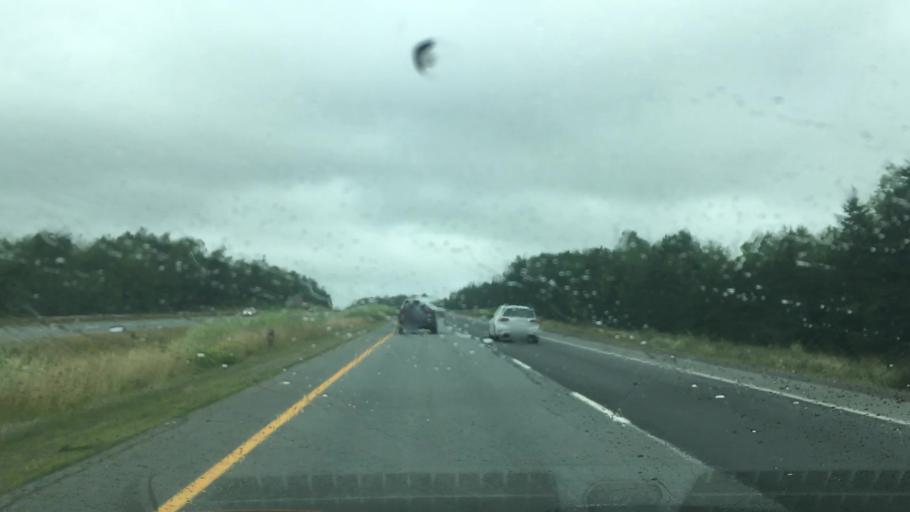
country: CA
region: Nova Scotia
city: Truro
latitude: 45.2638
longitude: -63.2922
